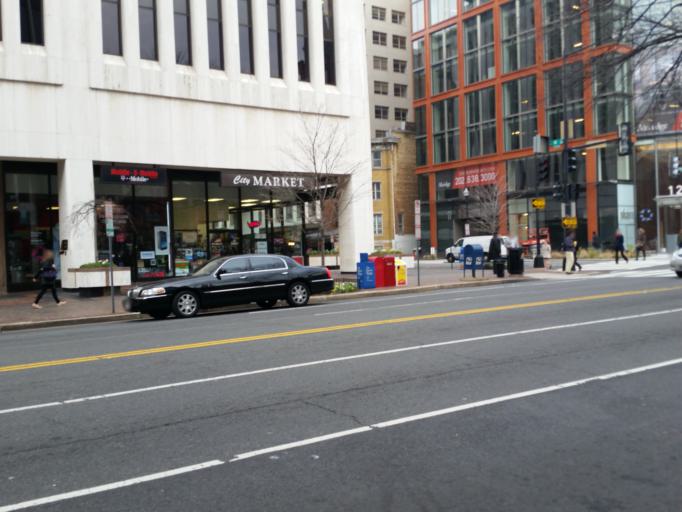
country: US
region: Washington, D.C.
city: Washington, D.C.
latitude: 38.9054
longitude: -77.0387
